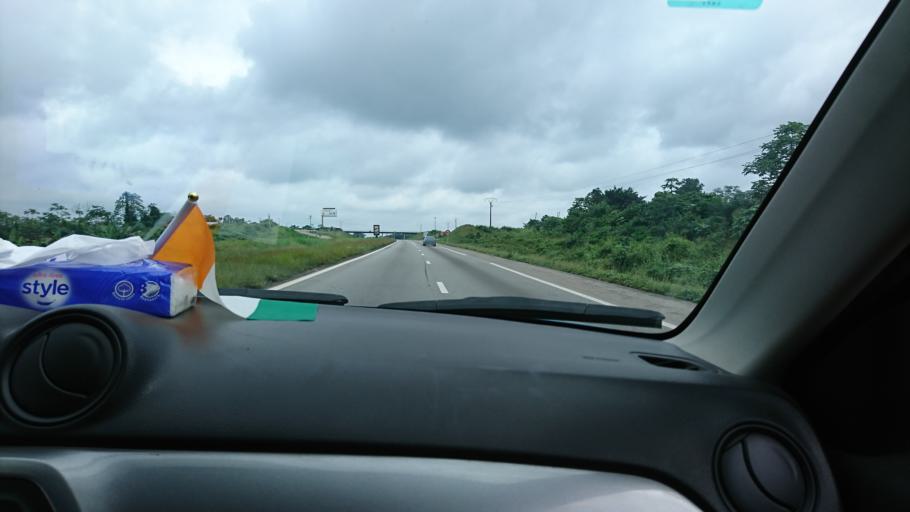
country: CI
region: Lagunes
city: Songon
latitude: 5.5196
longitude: -4.2878
